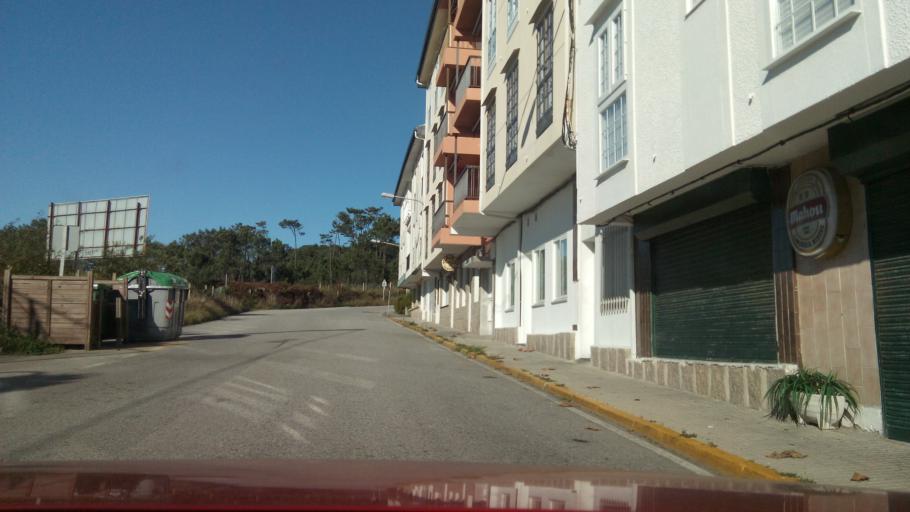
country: ES
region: Galicia
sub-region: Provincia de Pontevedra
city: O Grove
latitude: 42.4550
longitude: -8.9255
